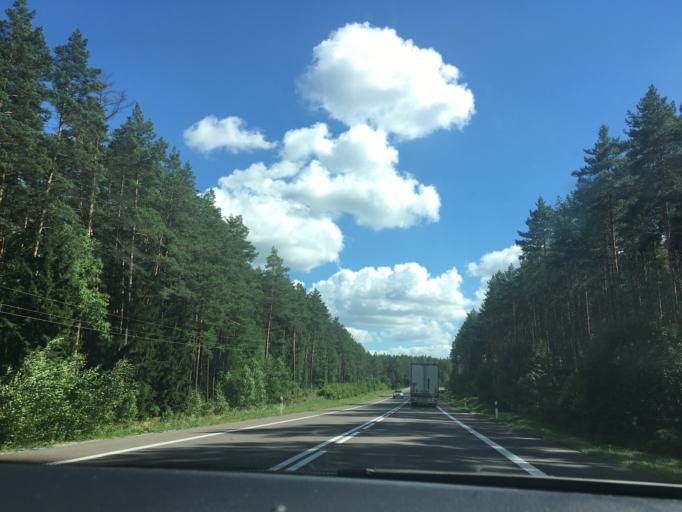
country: PL
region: Podlasie
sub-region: Powiat sokolski
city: Suchowola
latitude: 53.7291
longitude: 23.1049
